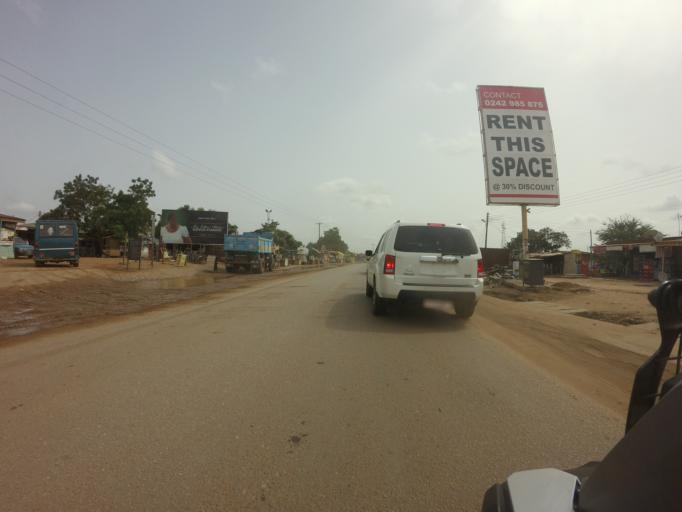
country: GH
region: Greater Accra
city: Tema
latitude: 5.7635
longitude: 0.0544
